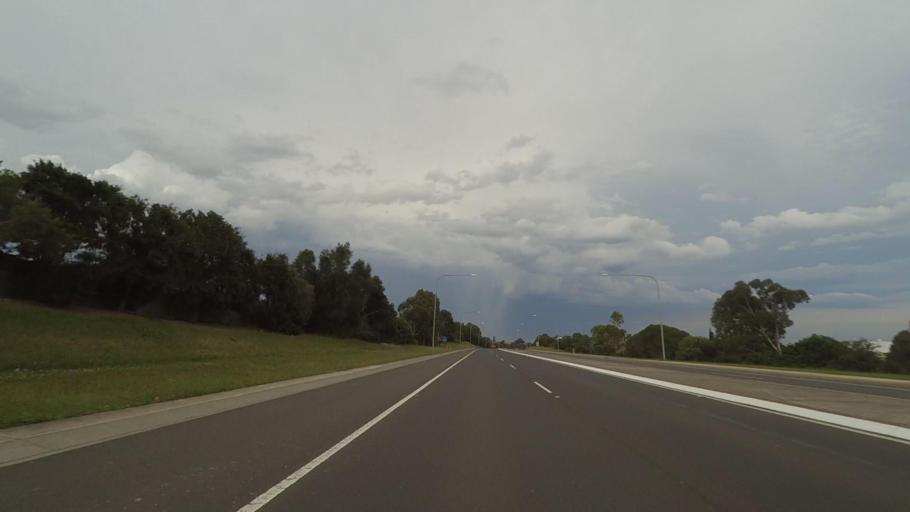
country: AU
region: New South Wales
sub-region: Shellharbour
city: Flinders
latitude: -34.5868
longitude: 150.8544
